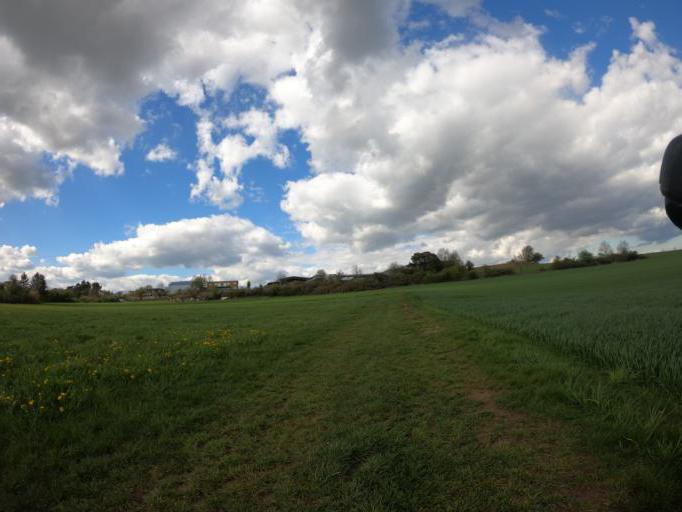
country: DE
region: Baden-Wuerttemberg
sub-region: Regierungsbezirk Stuttgart
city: Aidlingen
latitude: 48.7112
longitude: 8.9214
